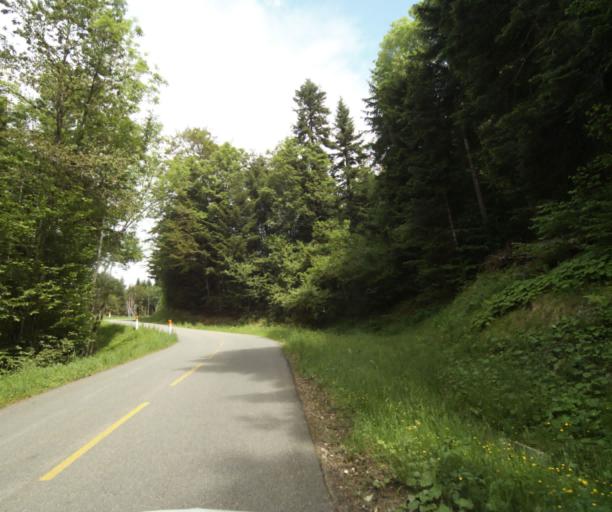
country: FR
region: Rhone-Alpes
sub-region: Departement de la Haute-Savoie
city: Bons-en-Chablais
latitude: 46.2645
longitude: 6.4258
